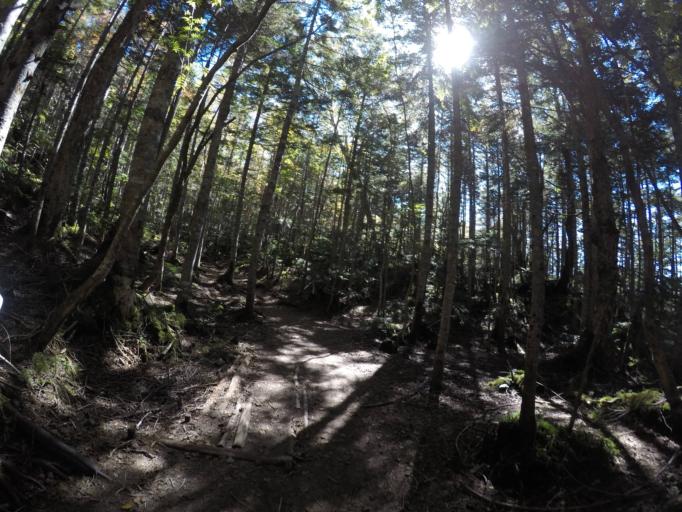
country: JP
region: Tochigi
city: Nikko
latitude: 36.8061
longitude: 139.3610
